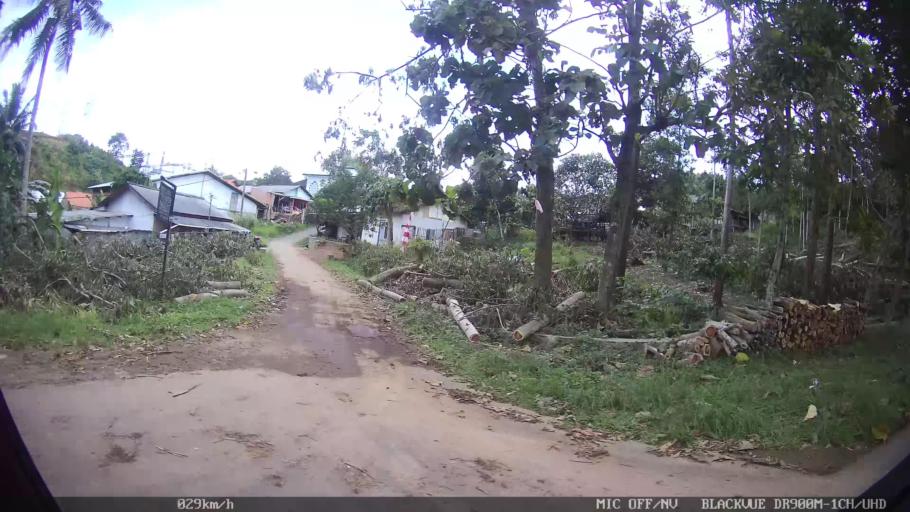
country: ID
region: Lampung
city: Bandarlampung
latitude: -5.4059
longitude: 105.1925
